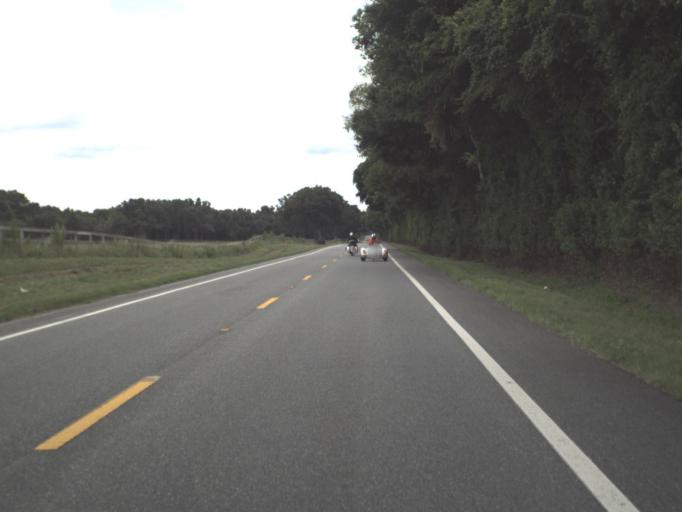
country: US
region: Florida
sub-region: Alachua County
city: Archer
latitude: 29.5809
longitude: -82.5518
